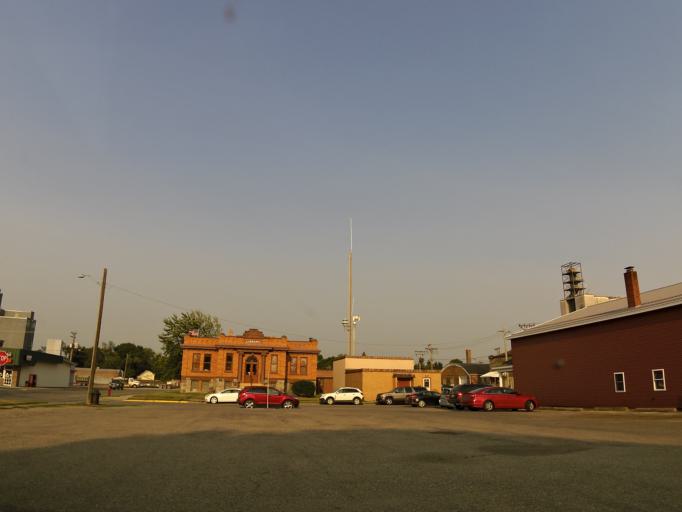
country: US
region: North Dakota
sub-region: Traill County
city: Mayville
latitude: 47.5009
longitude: -97.3271
